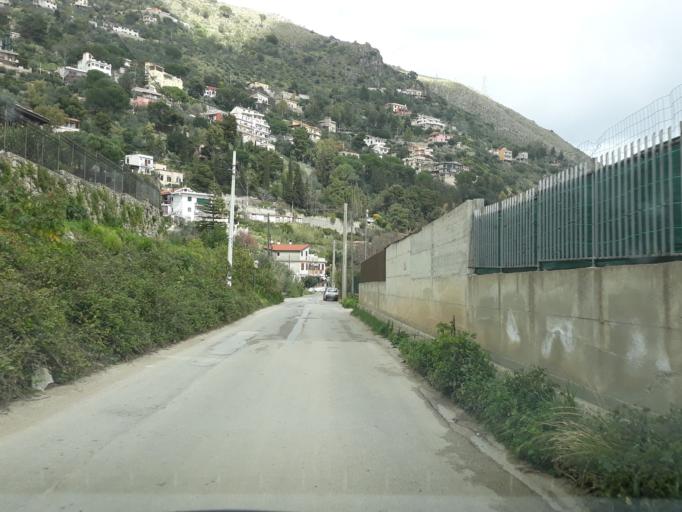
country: IT
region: Sicily
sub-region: Palermo
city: Monreale
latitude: 38.0847
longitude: 13.2979
